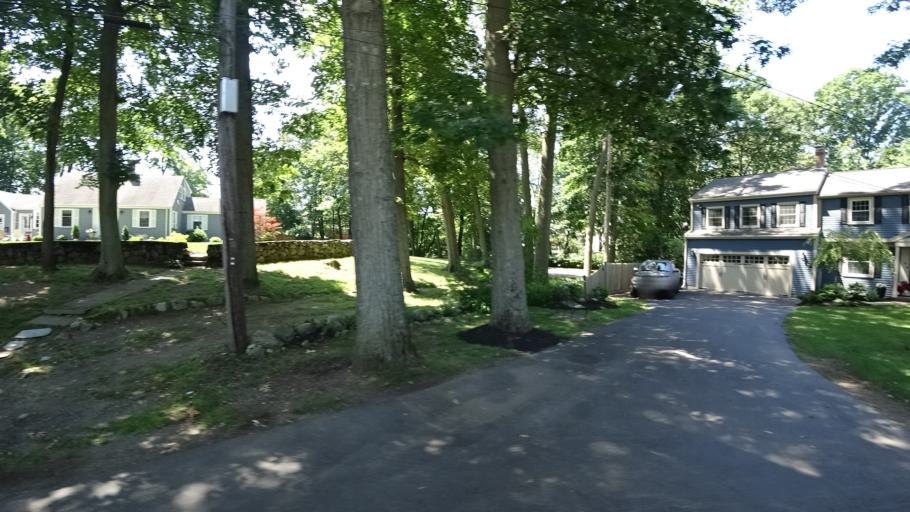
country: US
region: Massachusetts
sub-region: Norfolk County
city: Dedham
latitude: 42.2427
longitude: -71.1608
